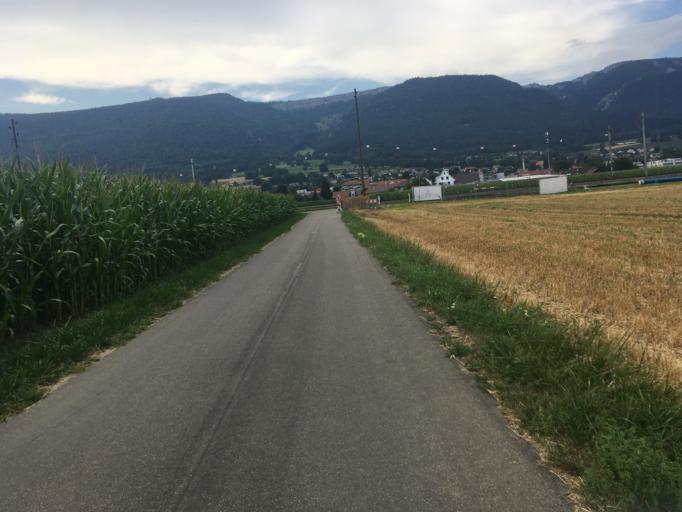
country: CH
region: Solothurn
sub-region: Bezirk Lebern
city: Bettlach
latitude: 47.1926
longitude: 7.4211
